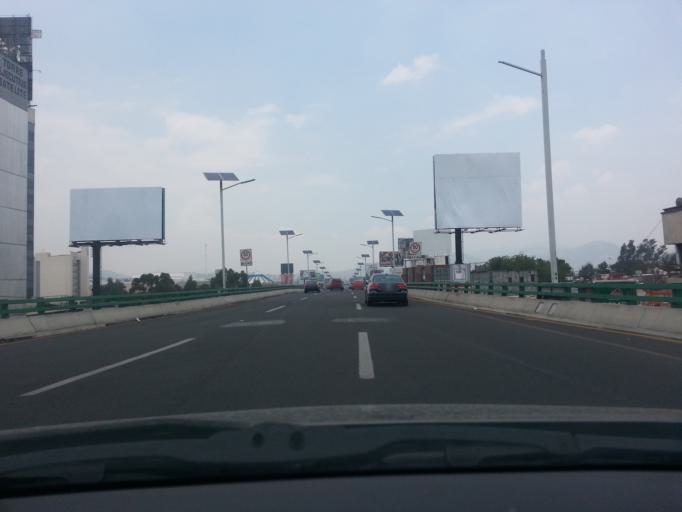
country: MX
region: Mexico
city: Vista Hermosa
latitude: 19.5201
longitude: -99.2295
